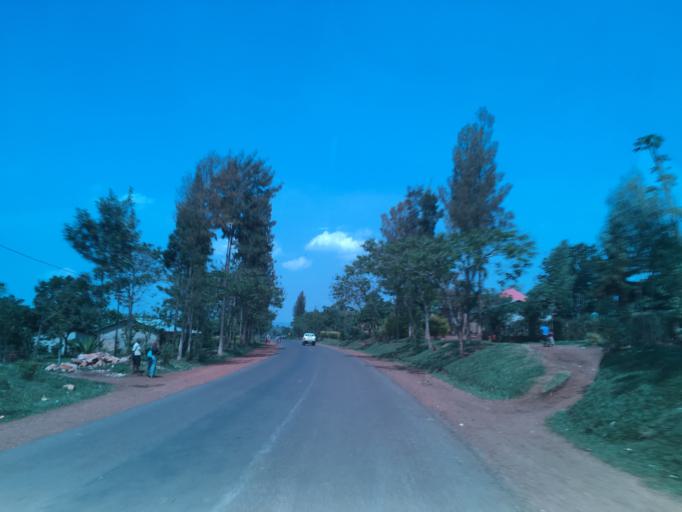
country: RW
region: Eastern Province
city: Rwamagana
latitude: -1.9119
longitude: 30.4981
